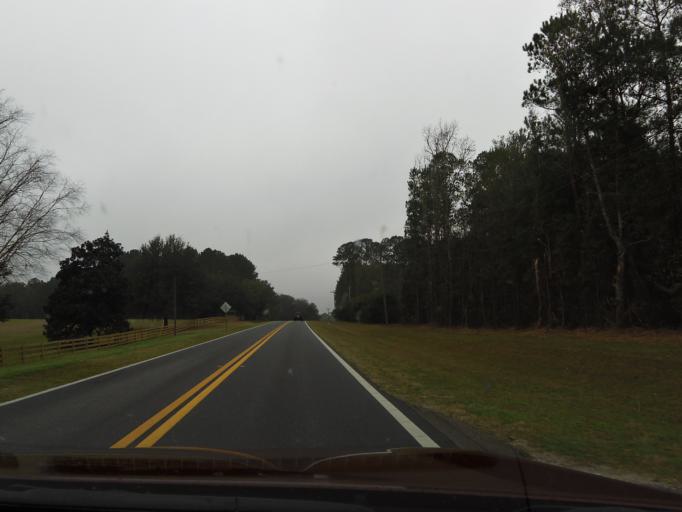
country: US
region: Florida
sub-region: Alachua County
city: High Springs
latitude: 29.8684
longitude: -82.5500
